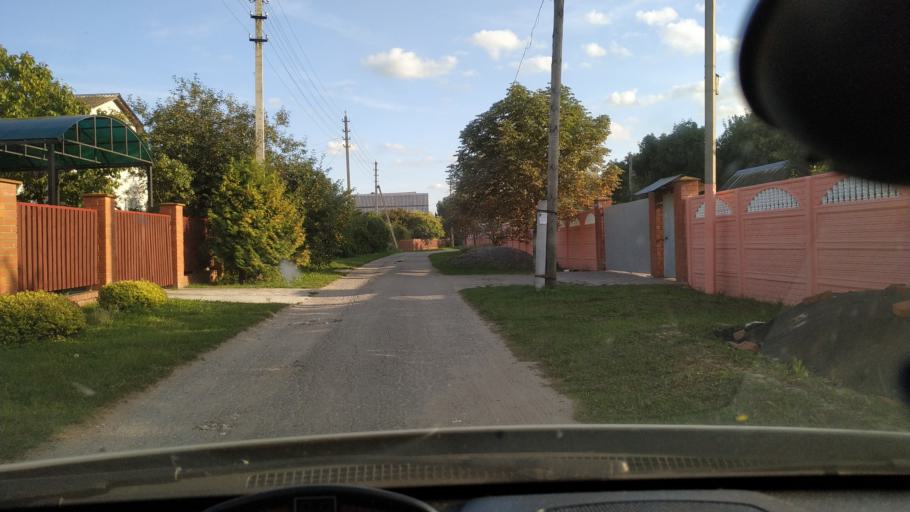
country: RU
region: Rjazan
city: Solotcha
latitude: 54.8687
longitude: 39.6699
